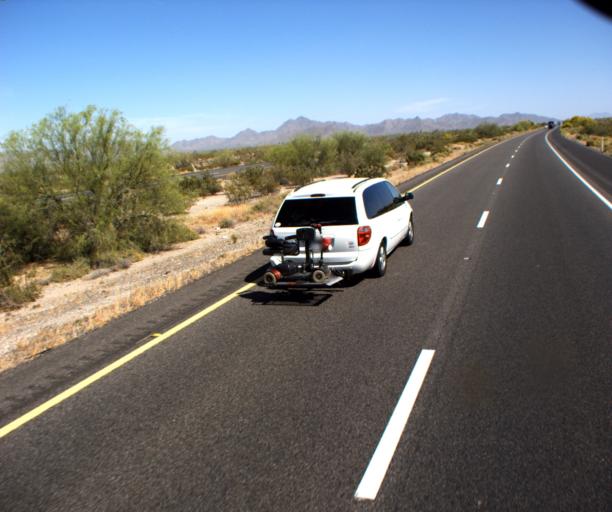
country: US
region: Arizona
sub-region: Maricopa County
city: Gila Bend
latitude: 32.9058
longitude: -112.5314
